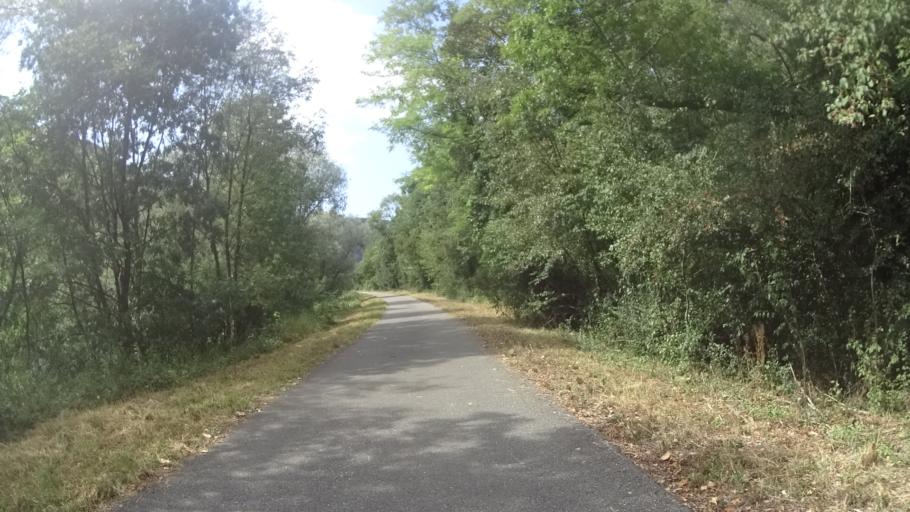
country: FR
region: Franche-Comte
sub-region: Departement du Doubs
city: Roulans
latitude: 47.2975
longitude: 6.2263
